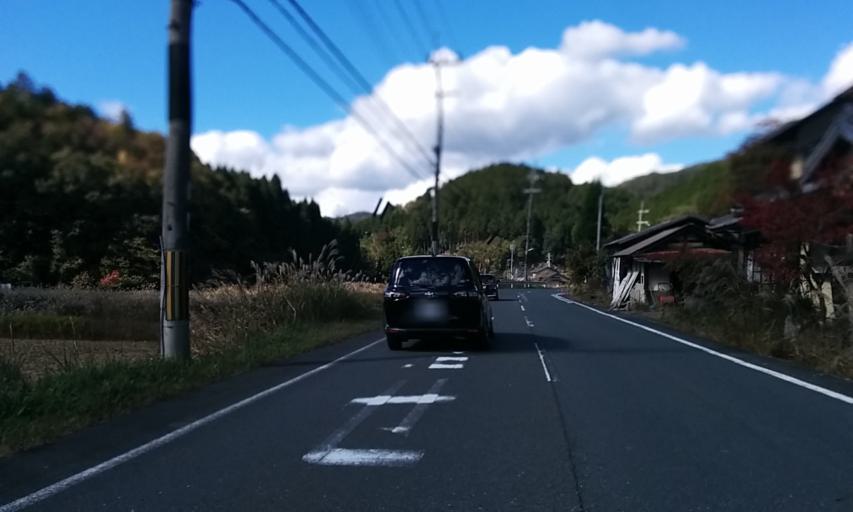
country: JP
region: Kyoto
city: Kameoka
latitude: 35.2085
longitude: 135.5737
